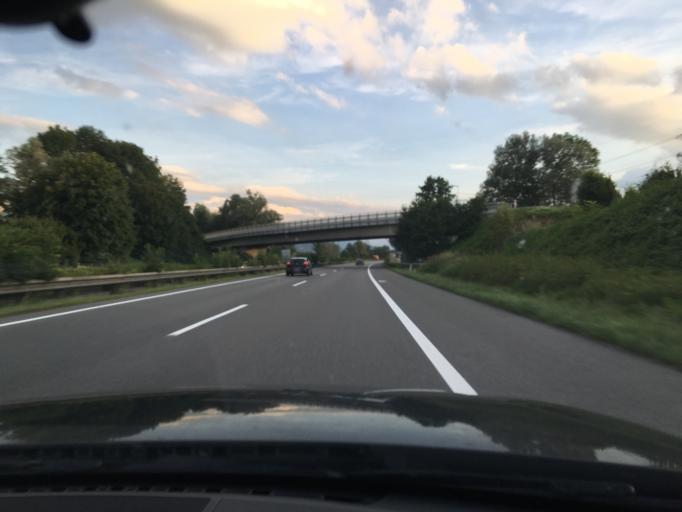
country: AT
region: Vorarlberg
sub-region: Politischer Bezirk Dornbirn
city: Dornbirn
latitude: 47.4296
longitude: 9.7190
